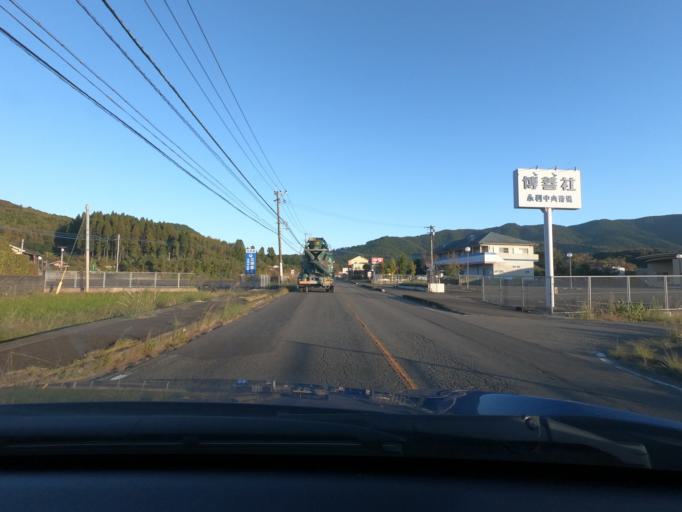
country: JP
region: Kagoshima
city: Satsumasendai
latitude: 31.8062
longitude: 130.3465
